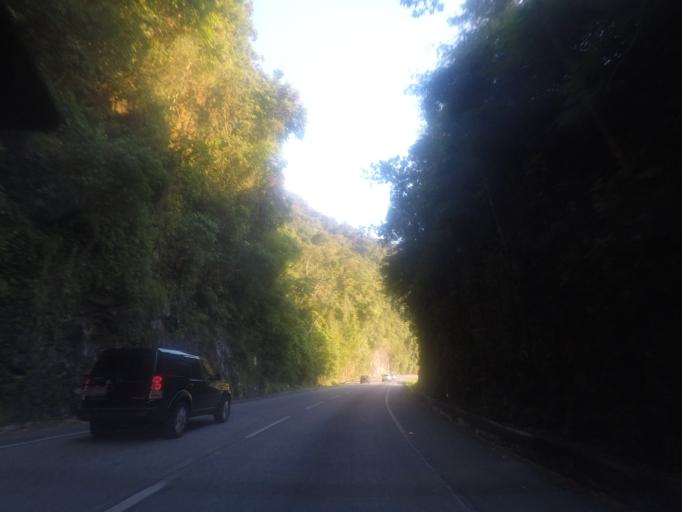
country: BR
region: Rio de Janeiro
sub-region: Petropolis
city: Petropolis
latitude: -22.5244
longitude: -43.2349
